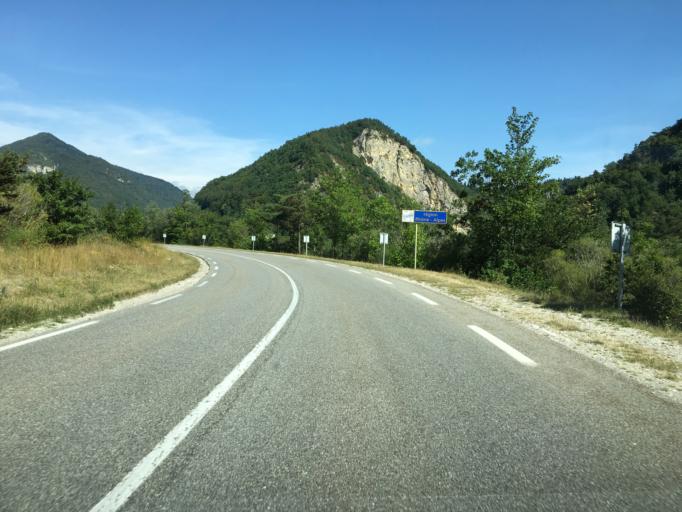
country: FR
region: Provence-Alpes-Cote d'Azur
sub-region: Departement des Hautes-Alpes
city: Veynes
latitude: 44.6473
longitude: 5.7025
